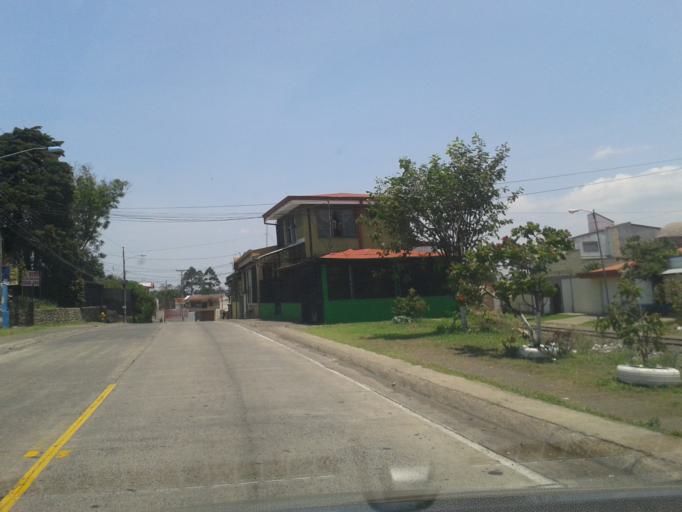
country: CR
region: Heredia
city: San Francisco
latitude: 9.9949
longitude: -84.1252
